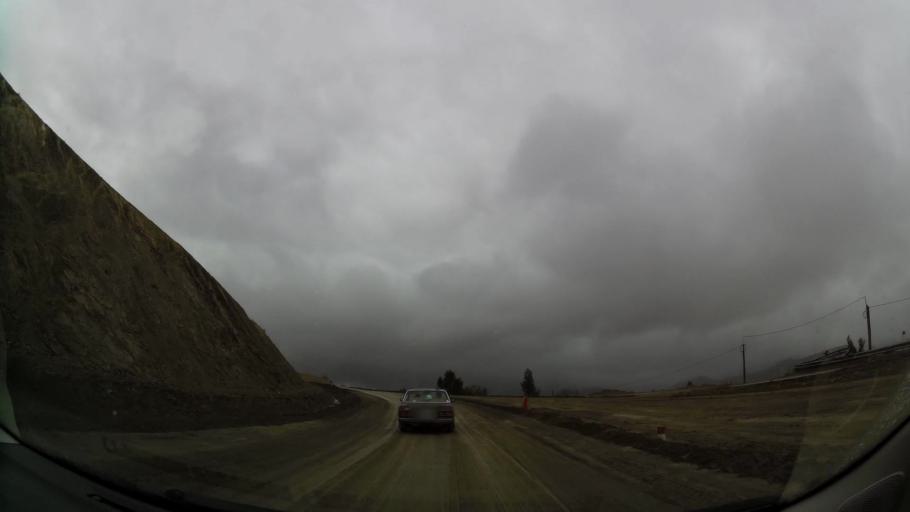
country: MA
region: Oriental
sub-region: Nador
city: Midar
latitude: 34.8967
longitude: -3.7734
